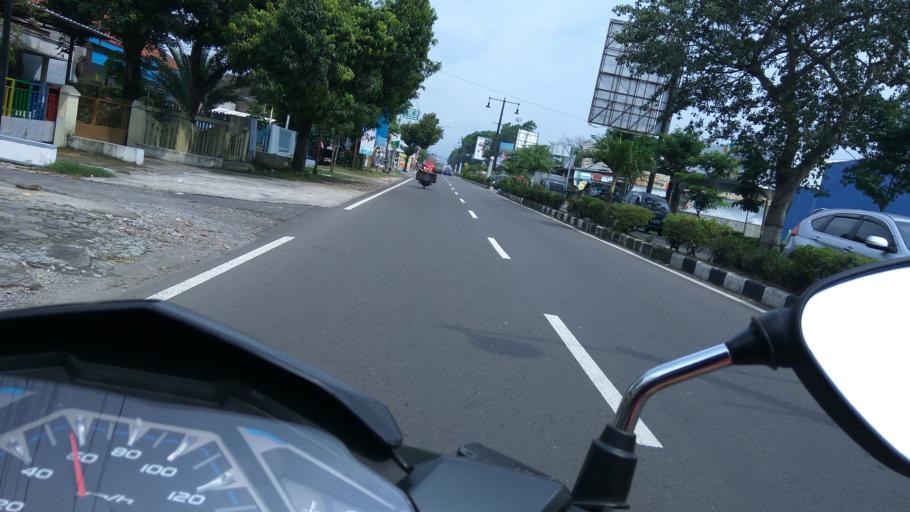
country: ID
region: Central Java
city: Jaten
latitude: -7.5890
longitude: 110.9248
